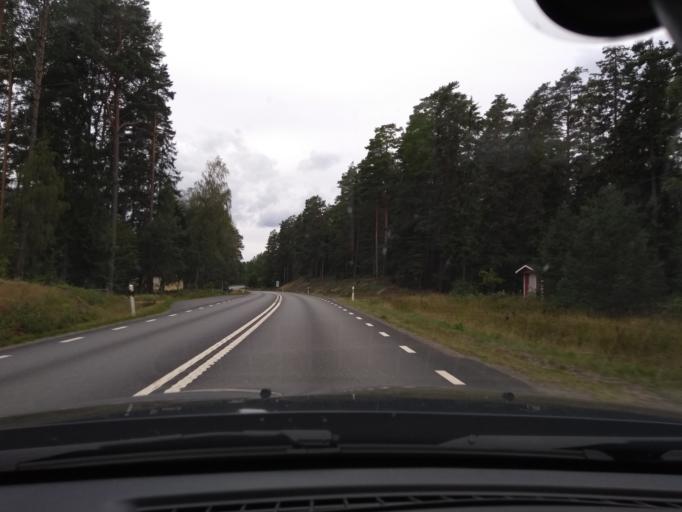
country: SE
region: Joenkoeping
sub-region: Eksjo Kommun
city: Haljarp
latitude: 57.6396
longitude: 15.3082
